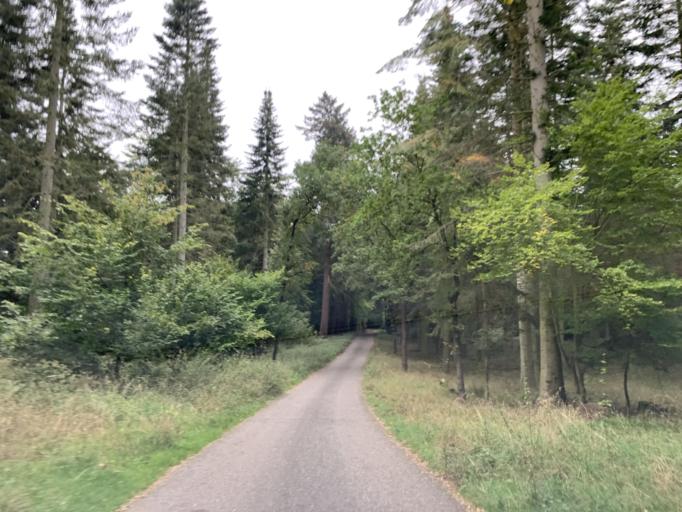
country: DE
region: Mecklenburg-Vorpommern
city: Woldegk
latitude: 53.3193
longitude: 13.6097
